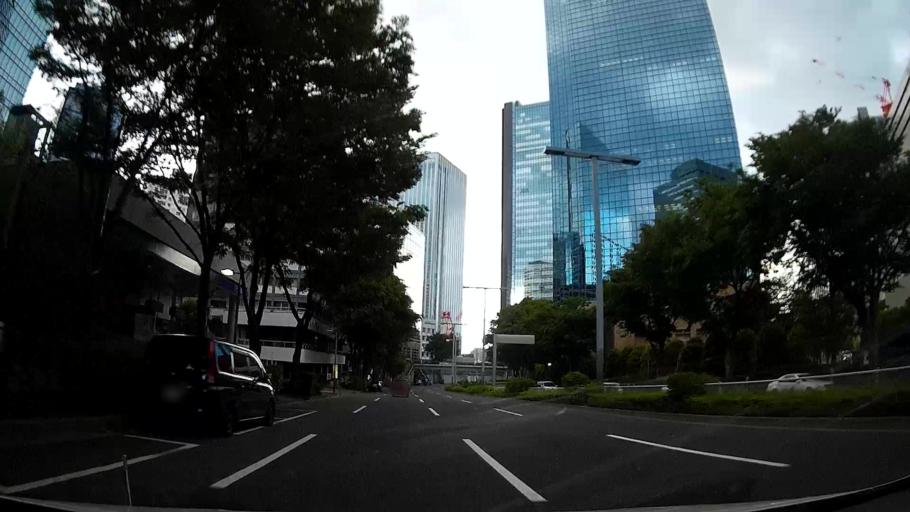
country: JP
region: Tokyo
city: Tokyo
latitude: 35.6923
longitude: 139.6902
